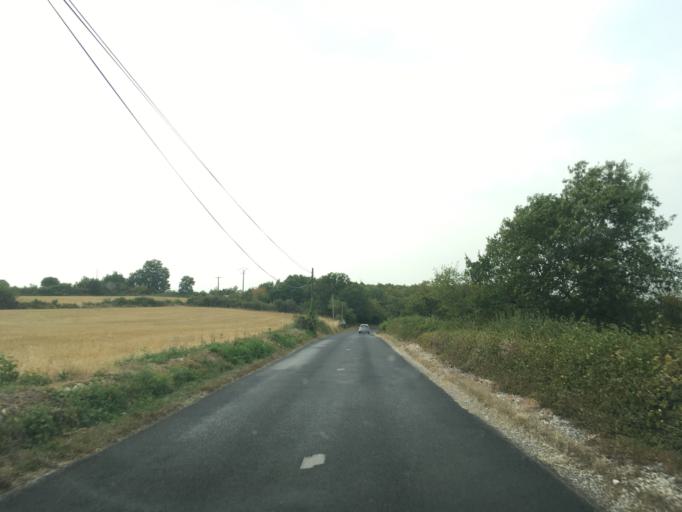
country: FR
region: Midi-Pyrenees
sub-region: Departement du Lot
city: Souillac
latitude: 44.8235
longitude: 1.5746
